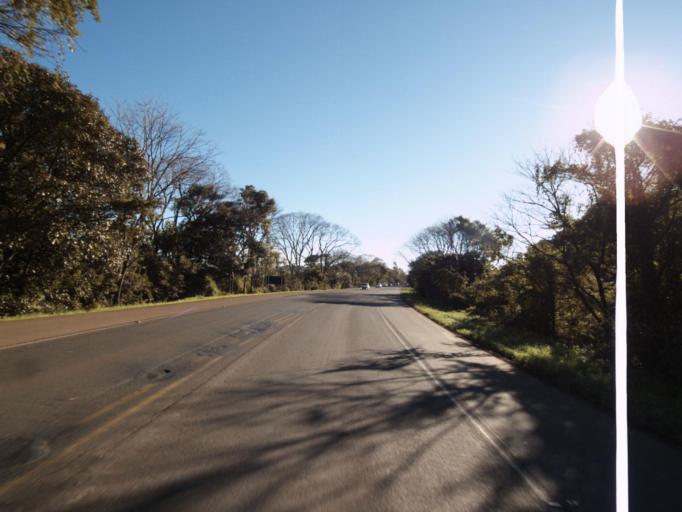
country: BR
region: Santa Catarina
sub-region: Chapeco
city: Chapeco
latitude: -27.0013
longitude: -52.7082
